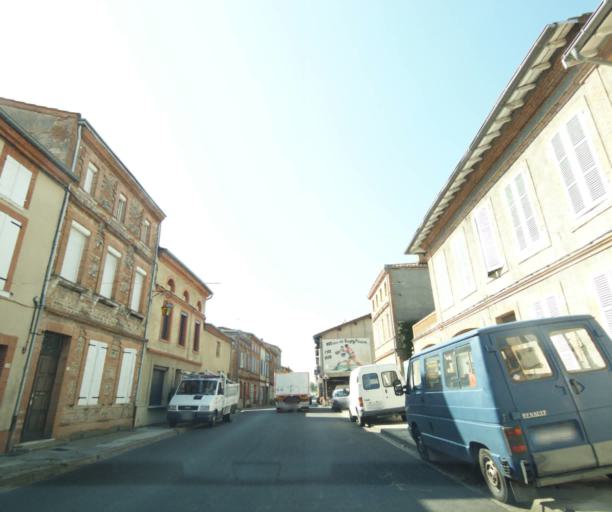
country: FR
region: Midi-Pyrenees
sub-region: Departement de la Haute-Garonne
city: Saint-Sulpice-sur-Leze
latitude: 43.3295
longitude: 1.3222
